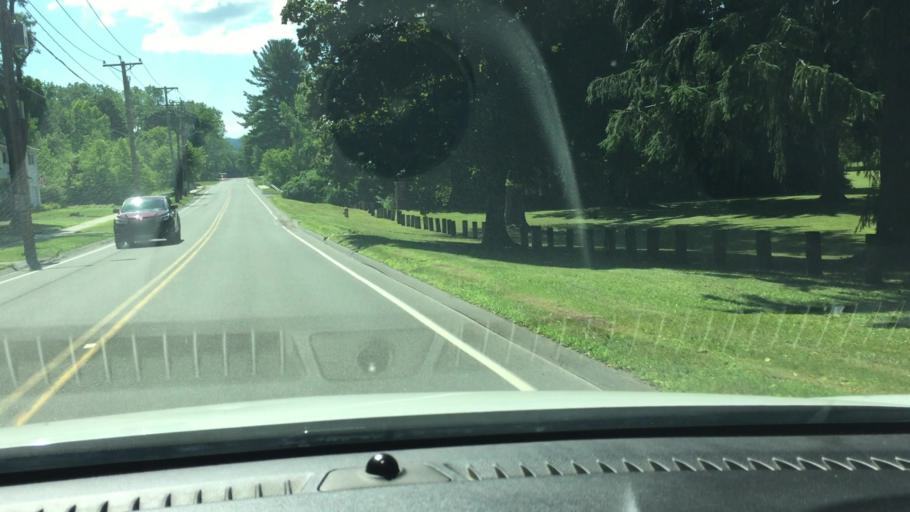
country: US
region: Massachusetts
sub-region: Berkshire County
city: Pittsfield
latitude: 42.4374
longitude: -73.2494
